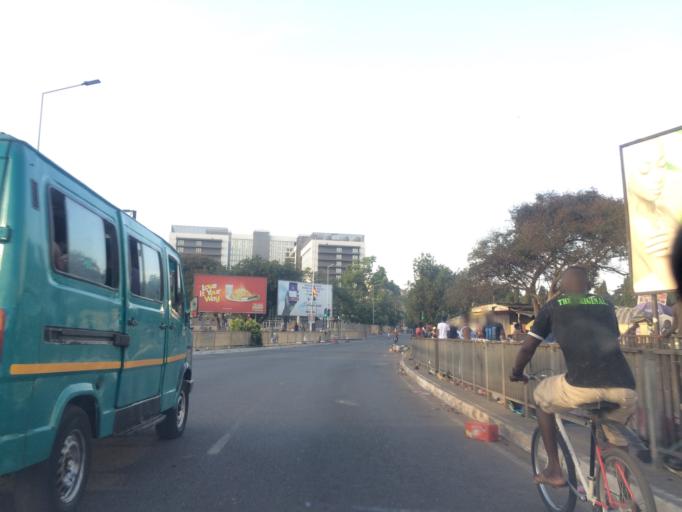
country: GH
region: Greater Accra
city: Accra
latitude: 5.5489
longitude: -0.2037
